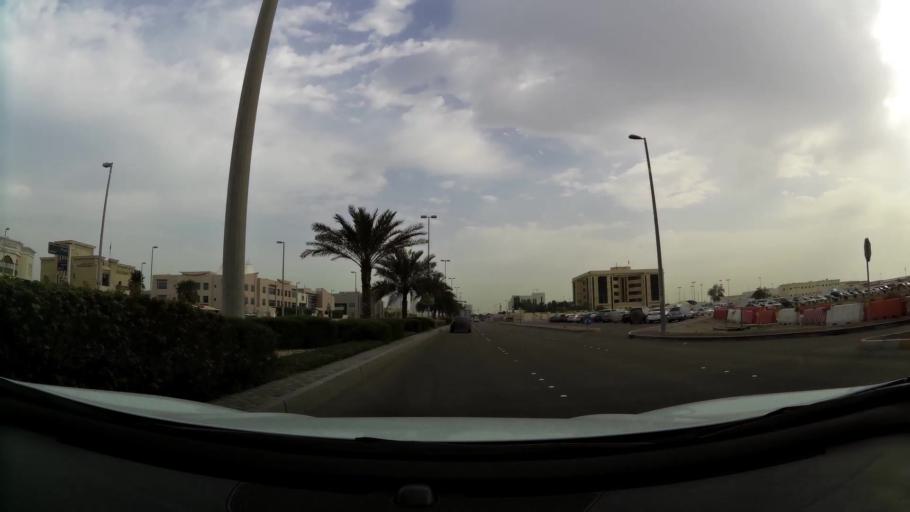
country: AE
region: Abu Dhabi
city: Abu Dhabi
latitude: 24.4686
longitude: 54.3842
